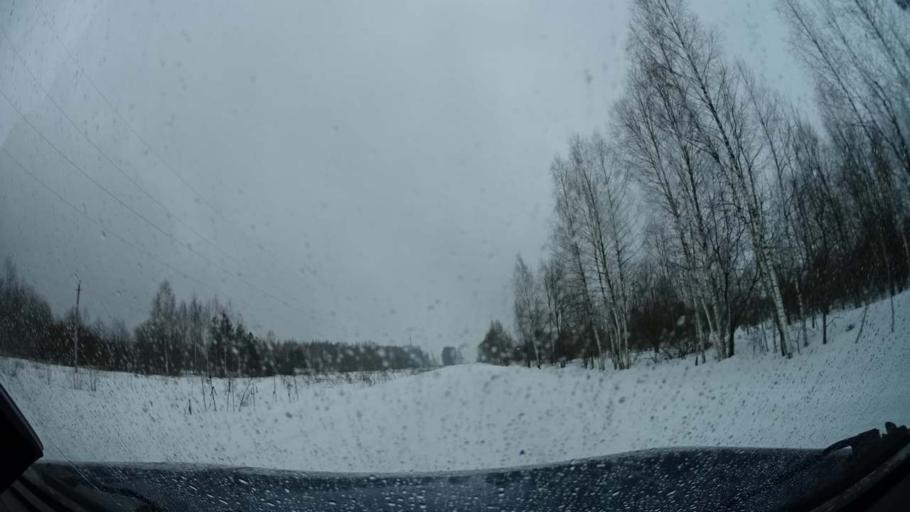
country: RU
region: Tverskaya
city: Konakovo
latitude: 56.7168
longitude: 36.6412
